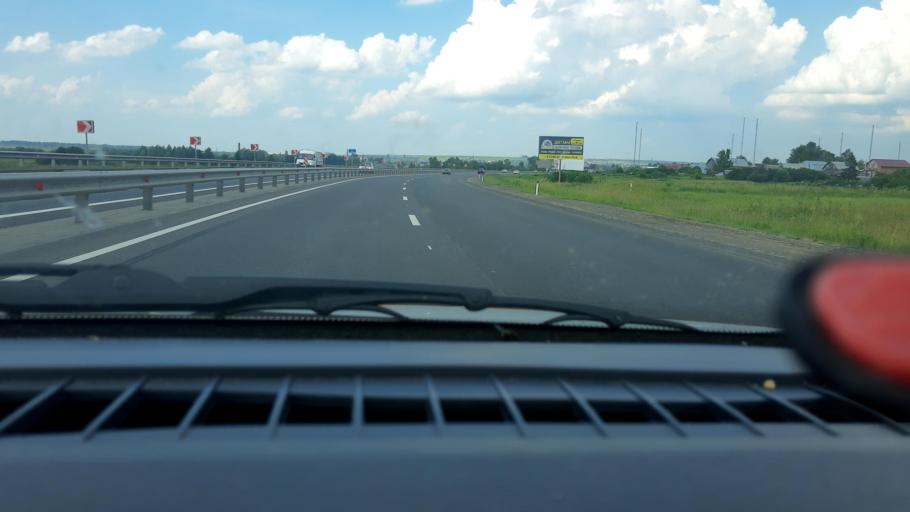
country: RU
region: Nizjnij Novgorod
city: Burevestnik
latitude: 56.1502
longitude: 43.9087
